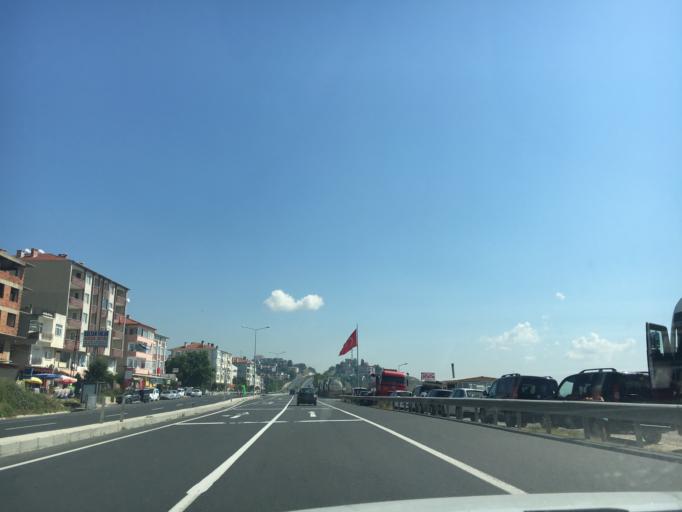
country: TR
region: Tekirdag
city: Sultankoy
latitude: 41.0174
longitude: 27.9888
